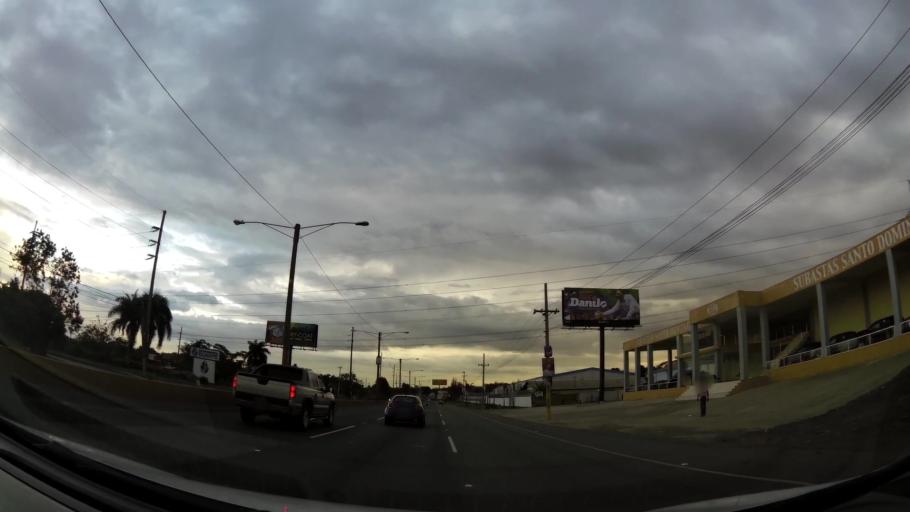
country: DO
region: Santo Domingo
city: Santo Domingo Oeste
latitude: 18.5545
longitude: -70.0563
